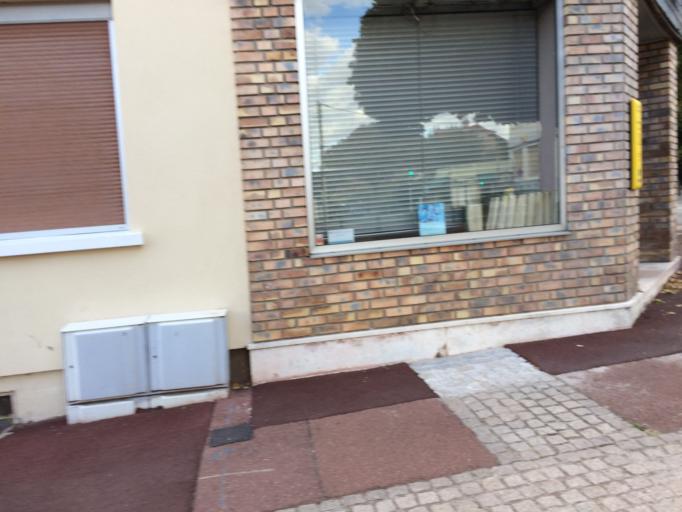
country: FR
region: Ile-de-France
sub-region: Departement de l'Essonne
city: Savigny-sur-Orge
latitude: 48.6792
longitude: 2.3453
